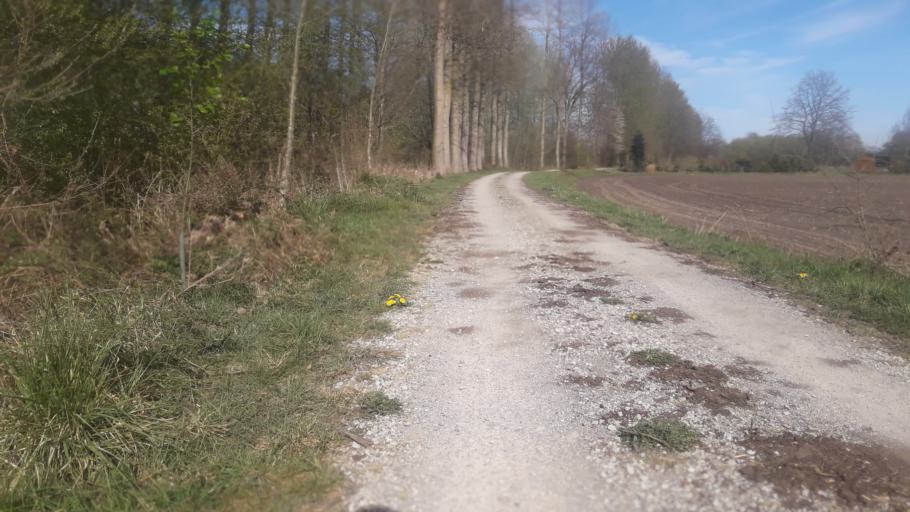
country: DE
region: North Rhine-Westphalia
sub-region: Regierungsbezirk Detmold
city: Delbruck
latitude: 51.7639
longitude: 8.6016
